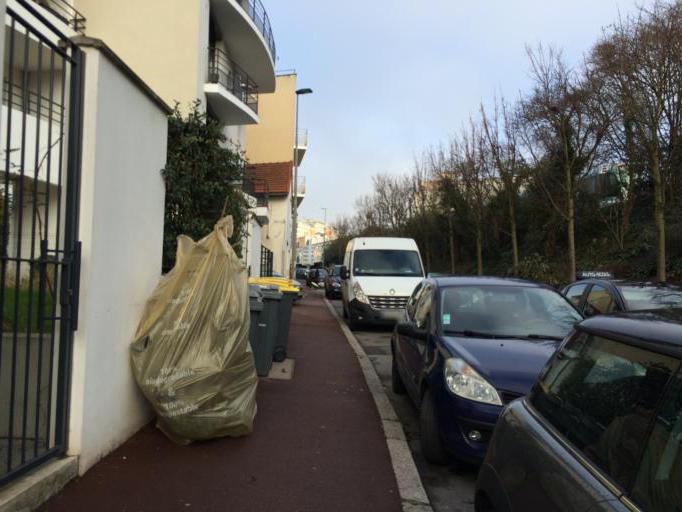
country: FR
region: Ile-de-France
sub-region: Departement des Hauts-de-Seine
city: Suresnes
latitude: 48.8664
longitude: 2.2215
